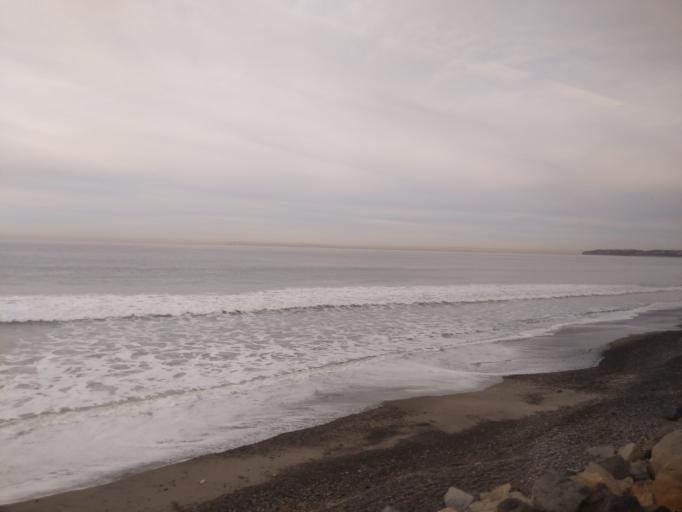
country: US
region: California
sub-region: Orange County
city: San Clemente
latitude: 33.4291
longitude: -117.6298
